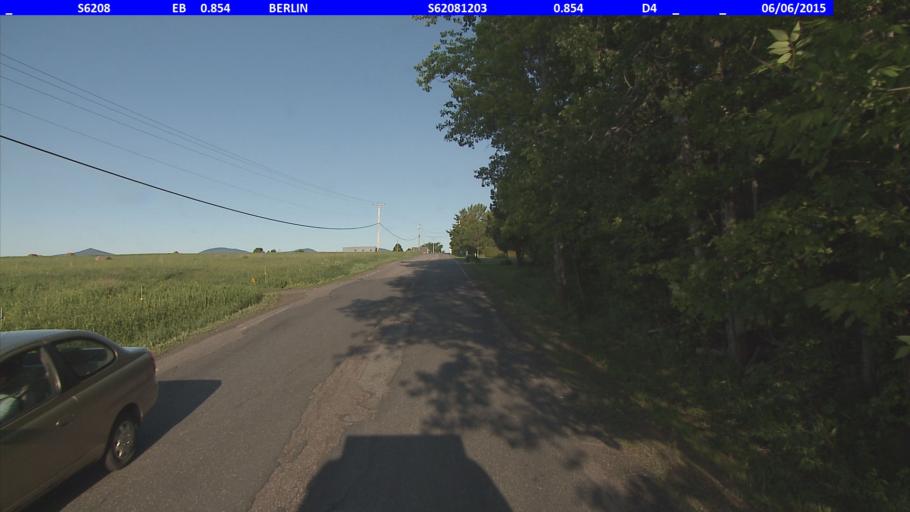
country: US
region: Vermont
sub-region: Washington County
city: Montpelier
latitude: 44.1993
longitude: -72.5741
